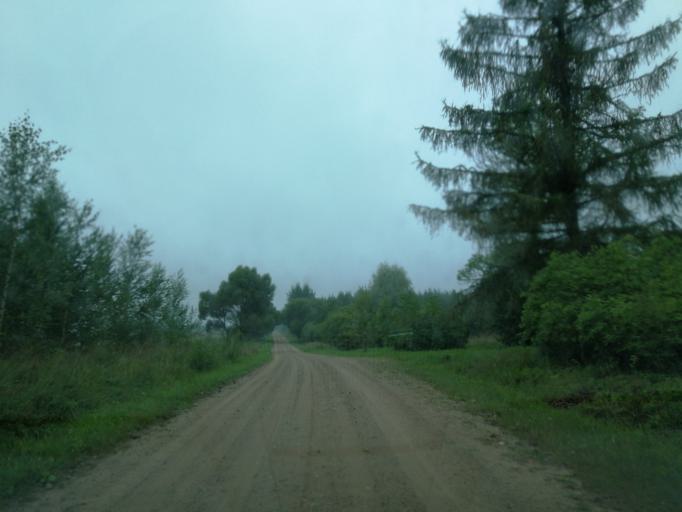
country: LV
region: Preilu Rajons
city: Jaunaglona
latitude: 56.3171
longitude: 27.0084
